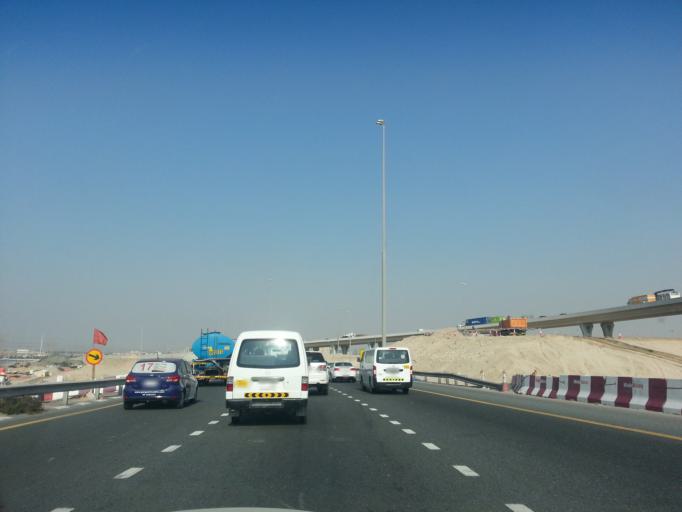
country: AE
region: Dubai
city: Dubai
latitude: 25.0161
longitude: 55.1589
